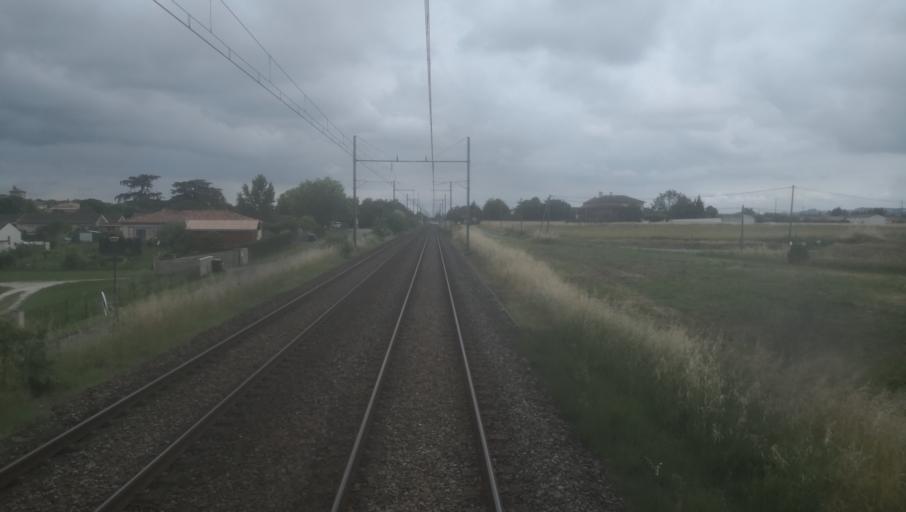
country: FR
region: Midi-Pyrenees
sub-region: Departement du Tarn-et-Garonne
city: Valence
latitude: 44.1016
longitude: 0.9388
